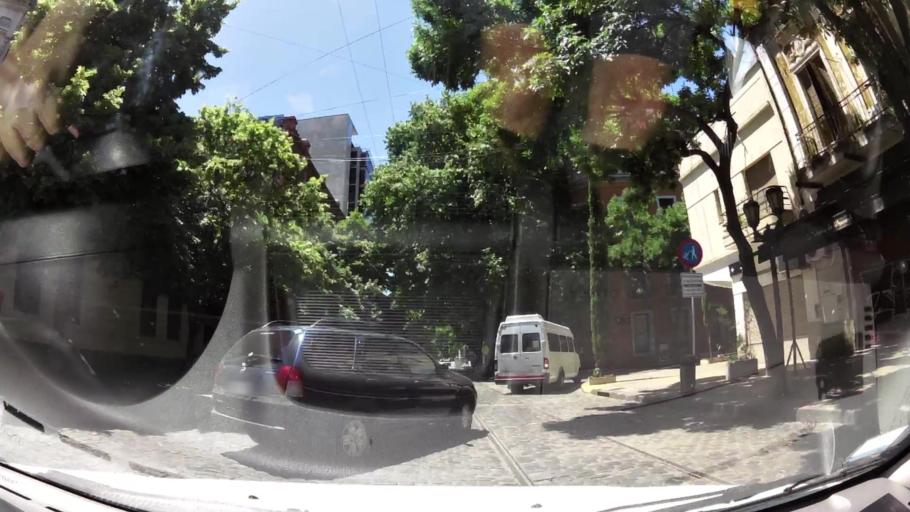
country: AR
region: Buenos Aires F.D.
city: Buenos Aires
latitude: -34.6159
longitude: -58.3705
